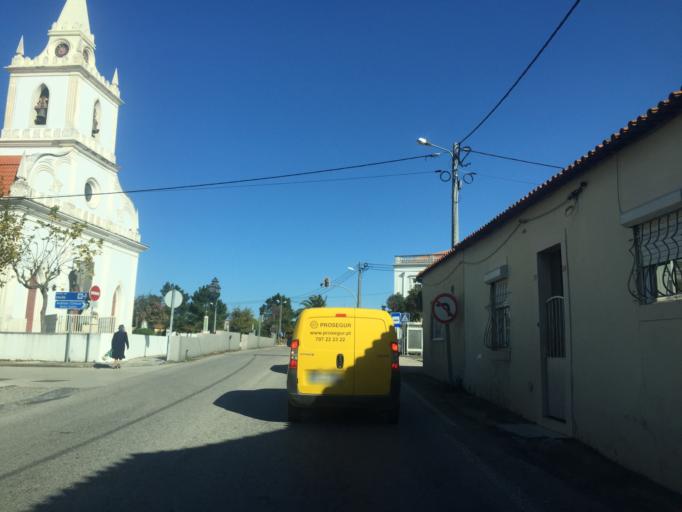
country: PT
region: Leiria
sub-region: Leiria
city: Monte Redondo
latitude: 39.8943
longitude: -8.8329
